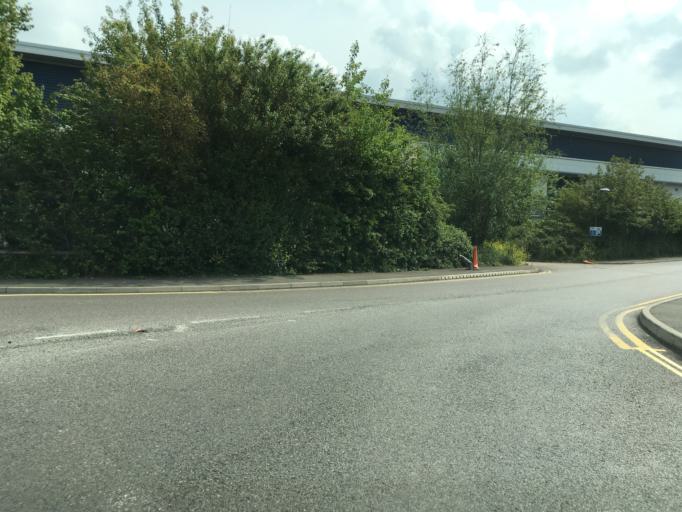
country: GB
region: England
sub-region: South Gloucestershire
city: Severn Beach
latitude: 51.5159
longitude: -2.6676
